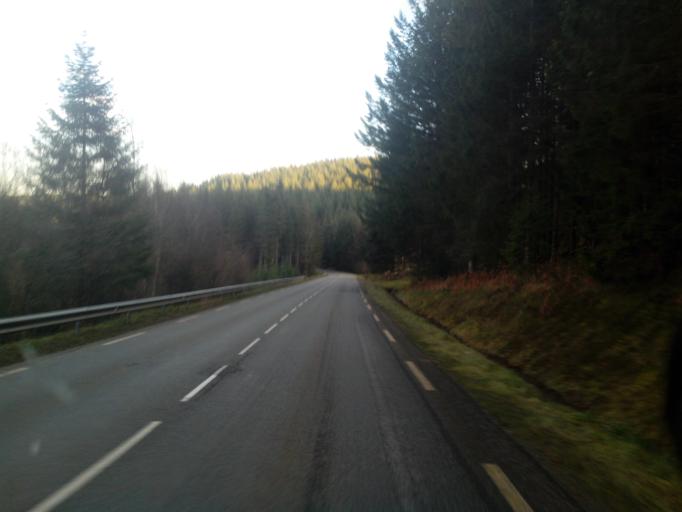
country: FR
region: Limousin
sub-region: Departement de la Correze
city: Meymac
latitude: 45.5797
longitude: 2.1183
